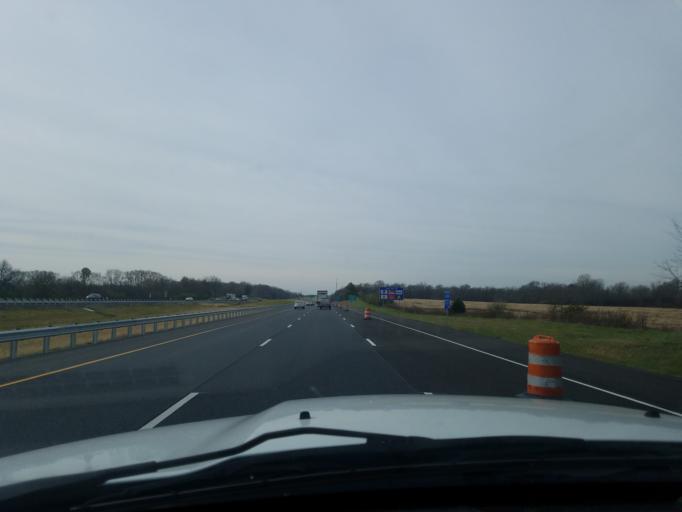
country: US
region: Indiana
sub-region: Hancock County
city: Fortville
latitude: 39.9914
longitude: -85.8905
